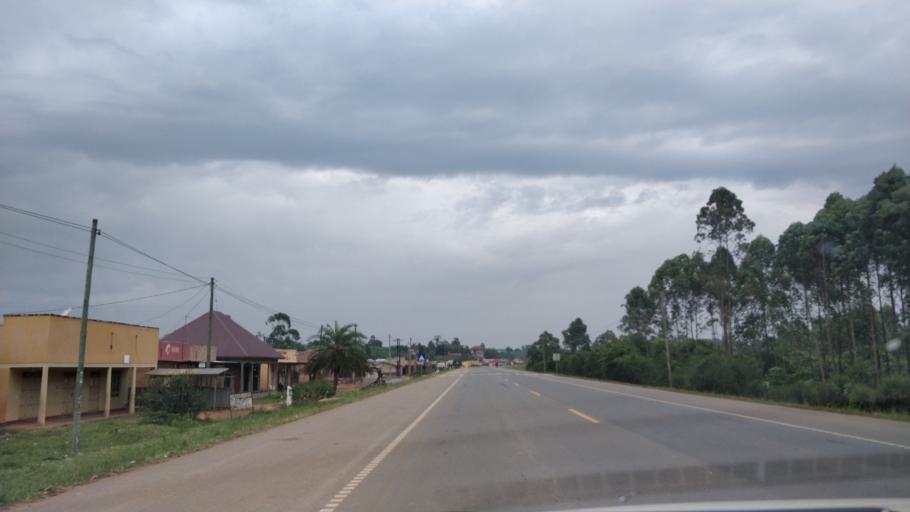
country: UG
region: Western Region
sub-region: Sheema District
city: Kibingo
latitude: -0.6626
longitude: 30.4527
